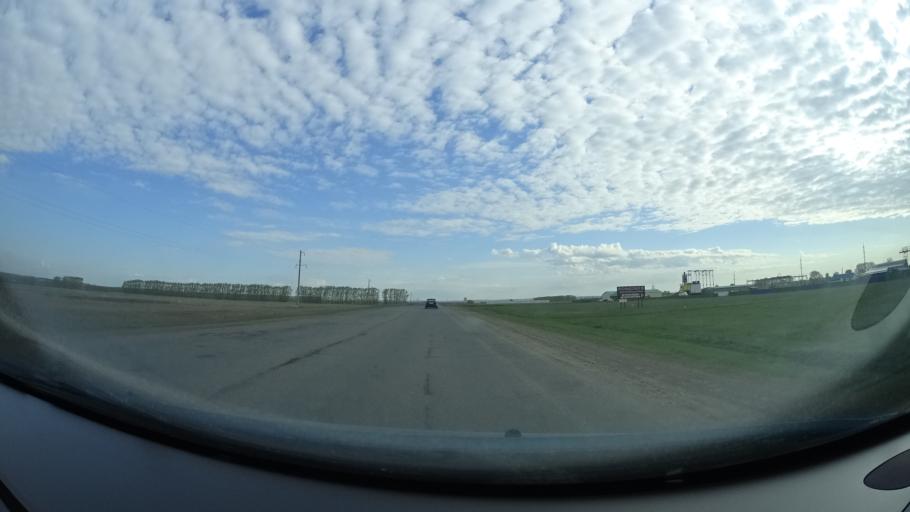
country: RU
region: Bashkortostan
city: Mikhaylovka
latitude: 54.9532
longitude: 55.7549
